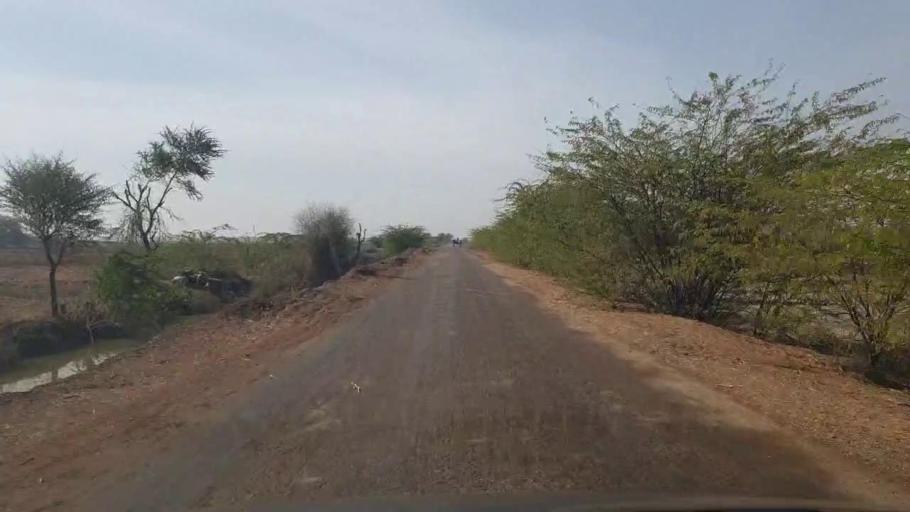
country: PK
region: Sindh
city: Umarkot
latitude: 25.3639
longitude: 69.6834
